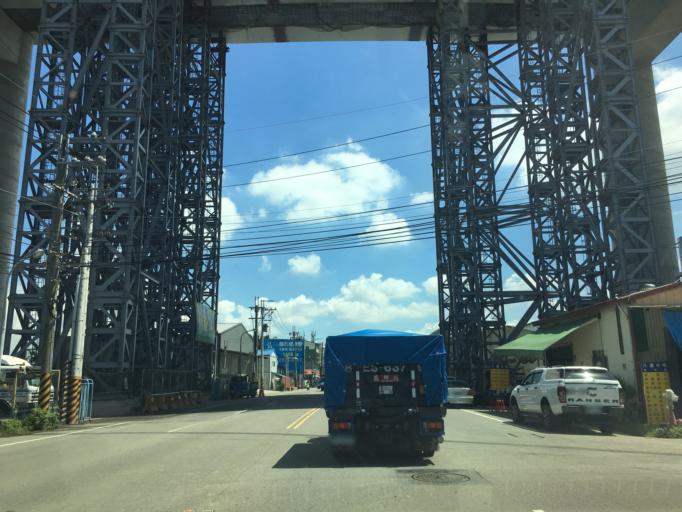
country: TW
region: Taiwan
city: Fengyuan
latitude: 24.2204
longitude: 120.7239
